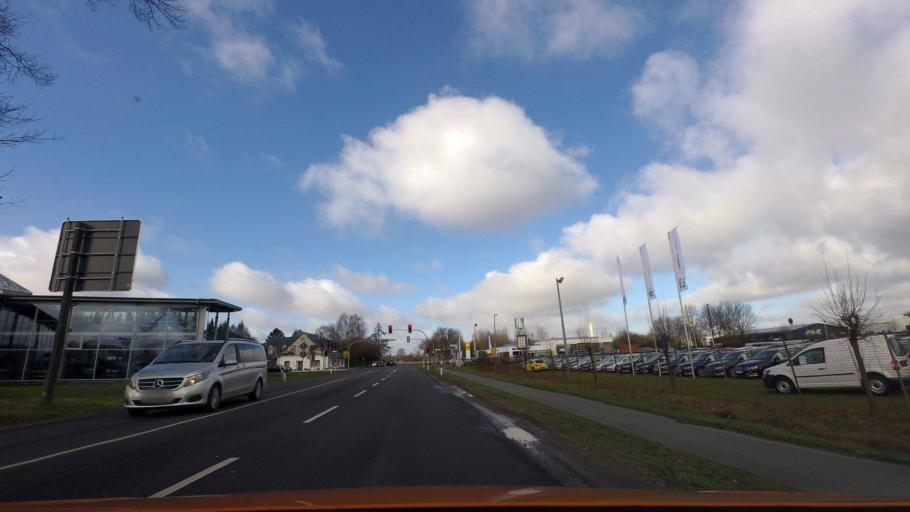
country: DE
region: Lower Saxony
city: Cappeln
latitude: 52.8295
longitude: 8.1163
